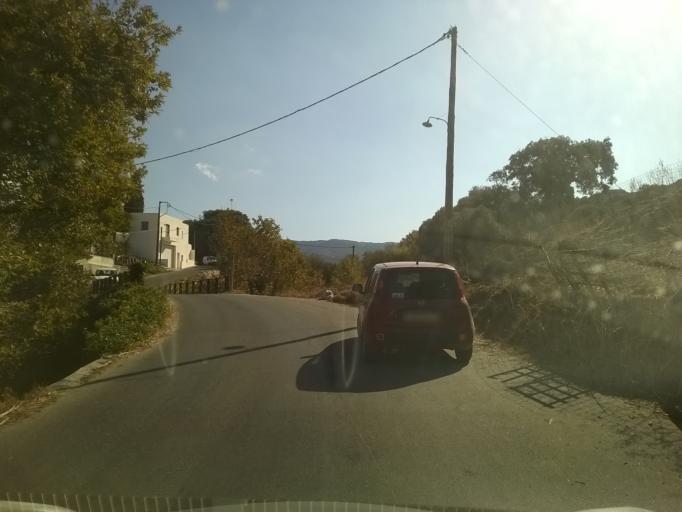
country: GR
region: South Aegean
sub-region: Nomos Kykladon
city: Filotion
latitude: 37.0999
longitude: 25.4785
